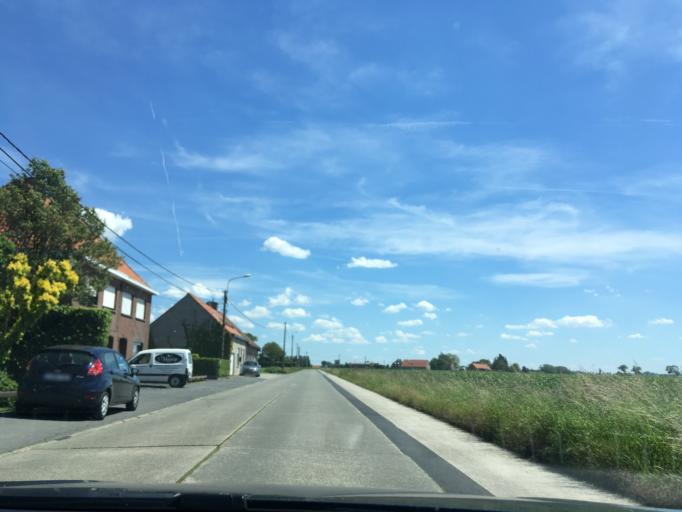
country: BE
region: Flanders
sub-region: Provincie West-Vlaanderen
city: Kortemark
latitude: 51.0228
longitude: 3.0650
